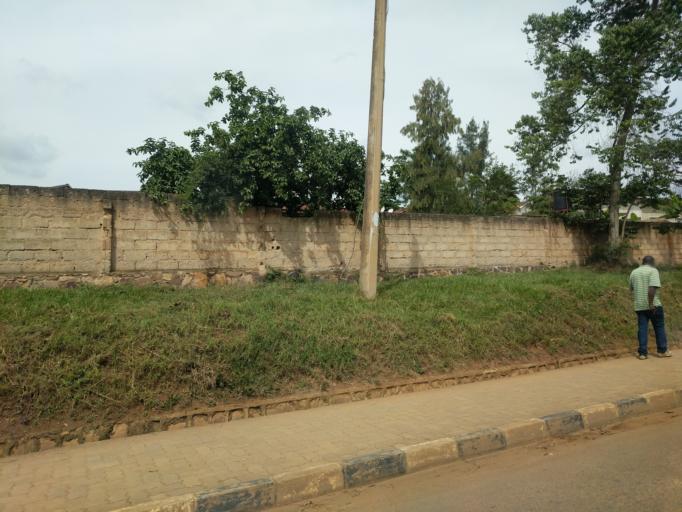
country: RW
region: Kigali
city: Kigali
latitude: -1.9703
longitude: 30.1303
